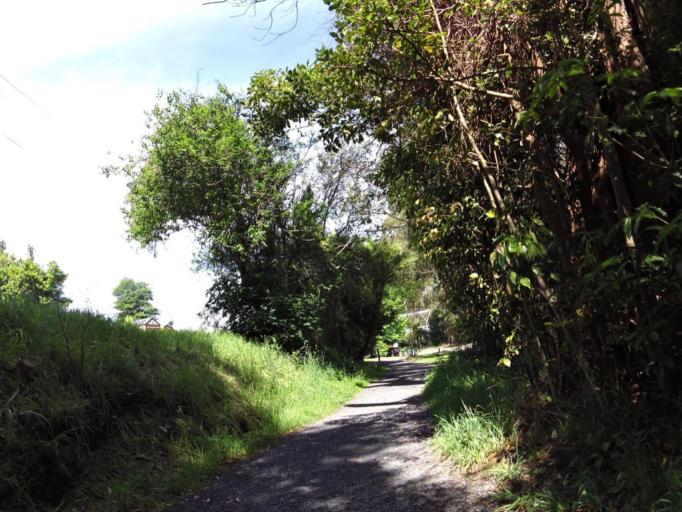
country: AU
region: Victoria
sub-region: Yarra Ranges
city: Millgrove
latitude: -37.7522
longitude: 145.6896
